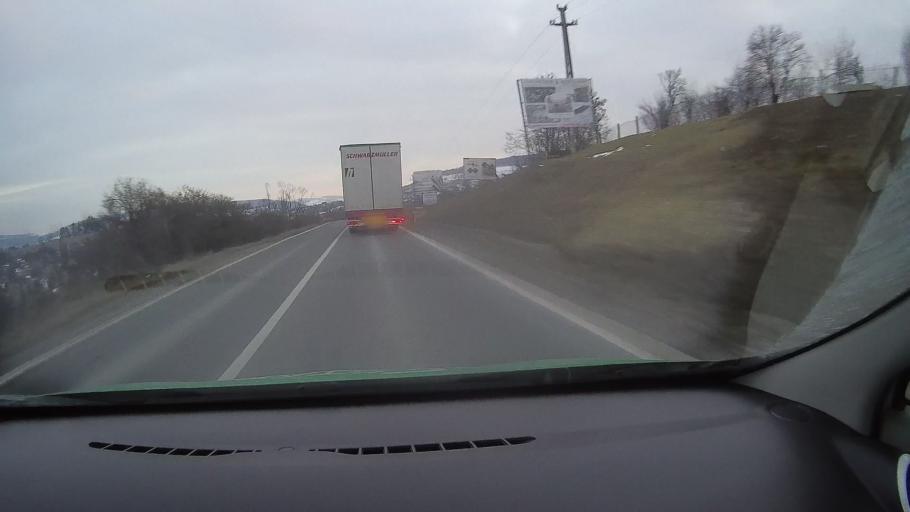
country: RO
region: Harghita
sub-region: Municipiul Odorheiu Secuiesc
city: Odorheiu Secuiesc
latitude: 46.3236
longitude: 25.2801
